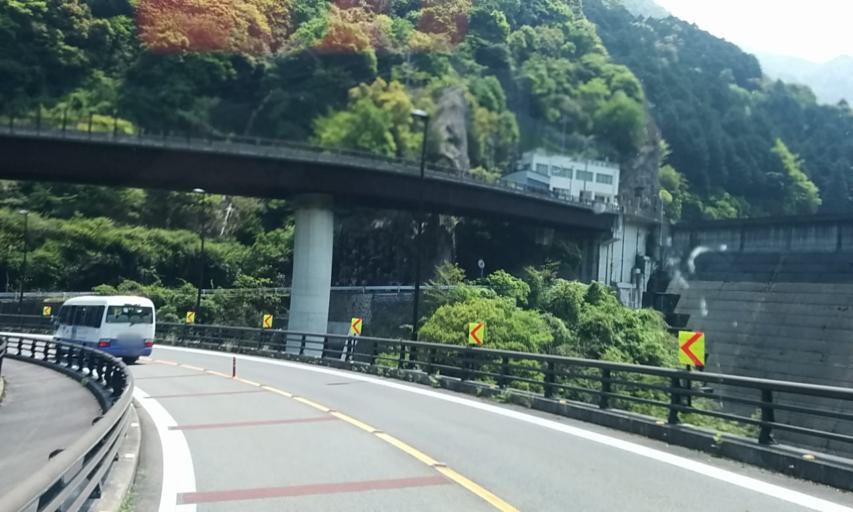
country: JP
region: Ehime
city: Niihama
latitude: 33.8948
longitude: 133.3094
